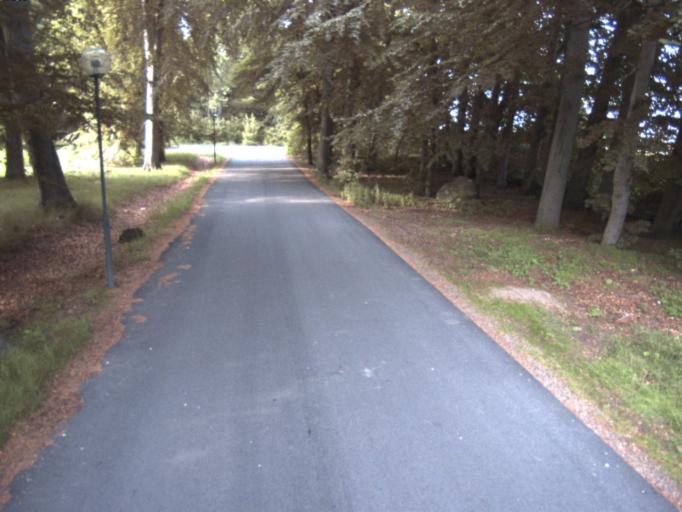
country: SE
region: Skane
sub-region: Helsingborg
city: Helsingborg
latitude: 56.0888
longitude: 12.6897
